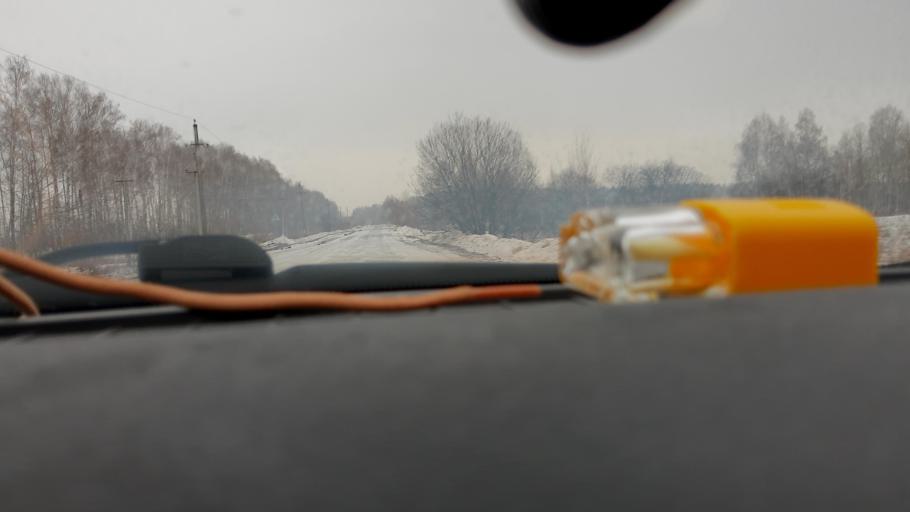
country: RU
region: Bashkortostan
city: Ulukulevo
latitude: 54.4966
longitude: 56.3987
